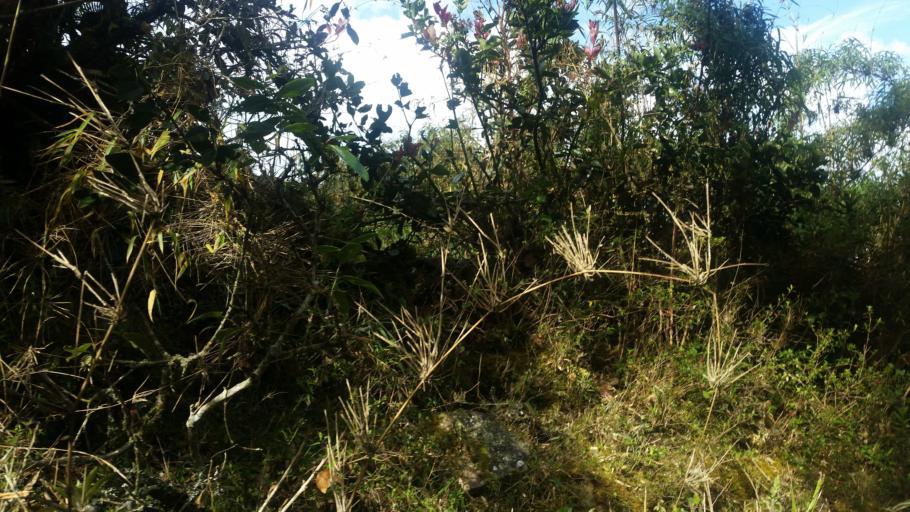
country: CO
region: Cundinamarca
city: Choachi
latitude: 4.5577
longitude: -73.9728
